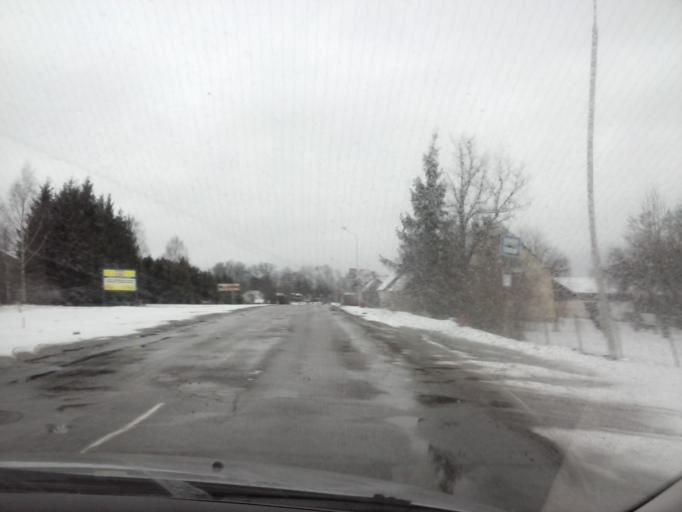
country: LV
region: Valkas Rajons
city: Valka
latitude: 57.7645
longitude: 26.0033
